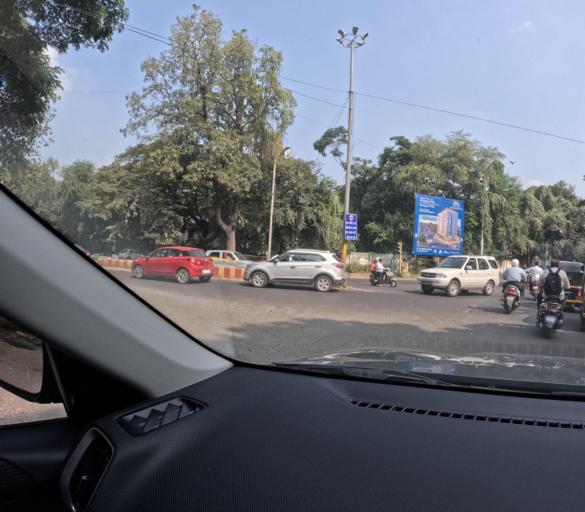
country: IN
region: Maharashtra
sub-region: Pune Division
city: Pune
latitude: 18.5233
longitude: 73.8877
